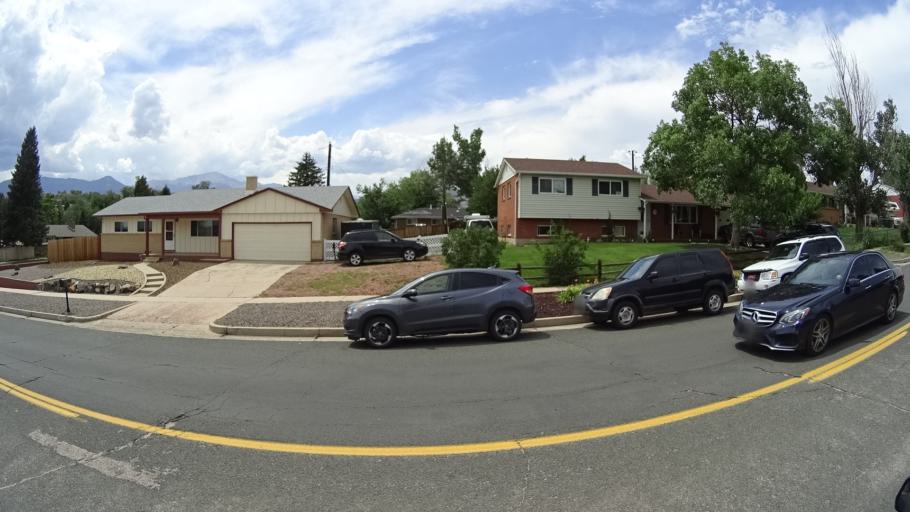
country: US
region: Colorado
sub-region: El Paso County
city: Colorado Springs
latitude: 38.8858
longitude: -104.8366
